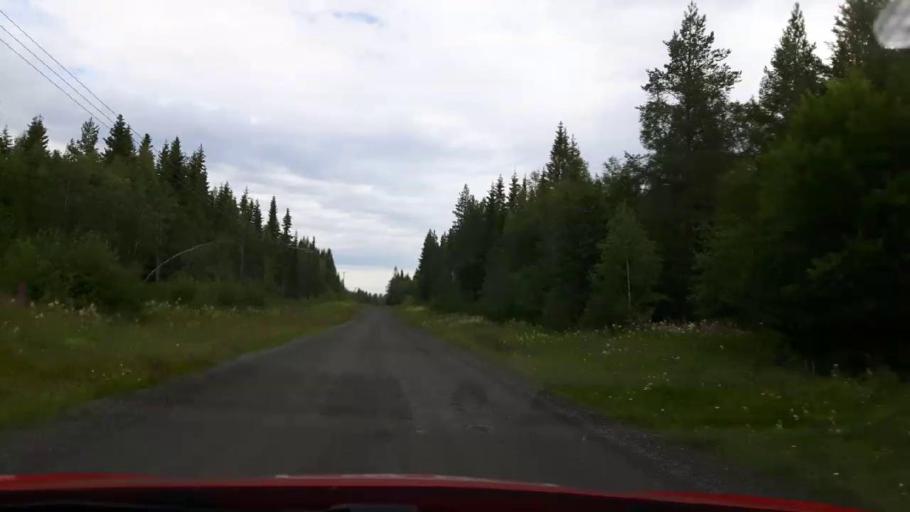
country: SE
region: Jaemtland
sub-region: Stroemsunds Kommun
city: Stroemsund
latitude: 63.5110
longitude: 15.3406
